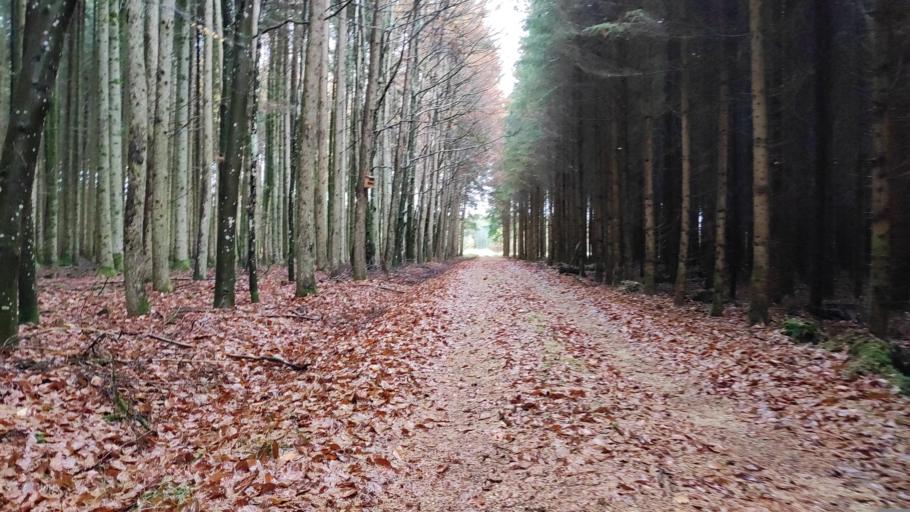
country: DE
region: Bavaria
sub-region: Swabia
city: Burtenbach
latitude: 48.3599
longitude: 10.5028
